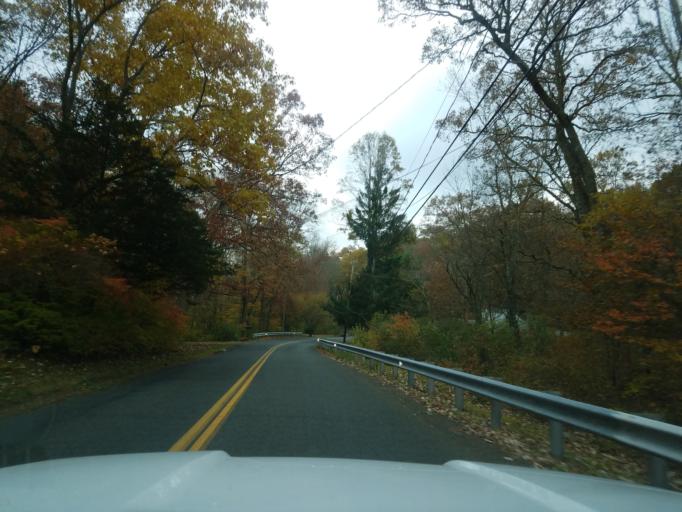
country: US
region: Connecticut
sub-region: New Haven County
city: Middlebury
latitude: 41.5108
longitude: -73.1593
